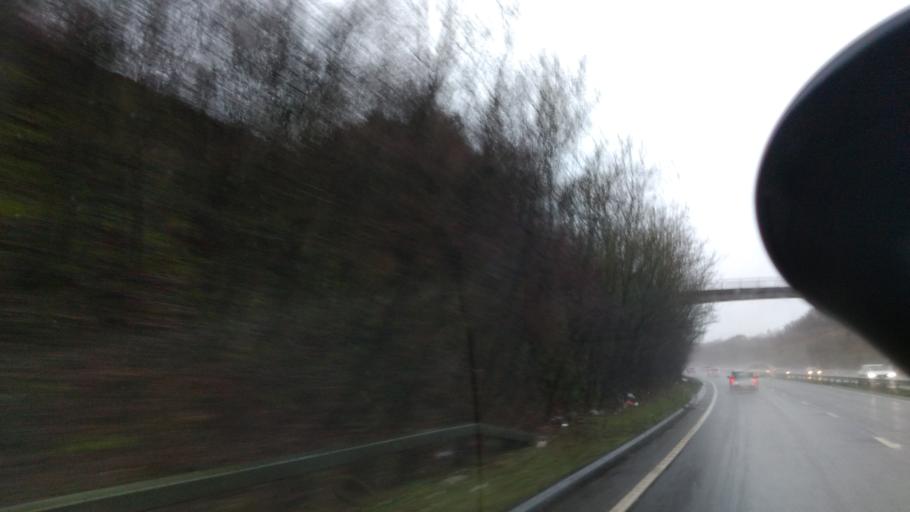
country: GB
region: England
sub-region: Brighton and Hove
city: Brighton
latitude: 50.8654
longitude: -0.1075
